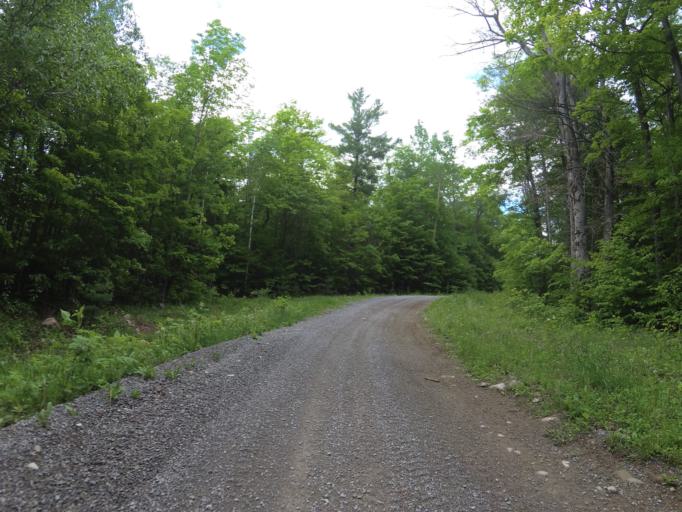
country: CA
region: Ontario
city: Renfrew
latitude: 45.1163
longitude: -76.8861
